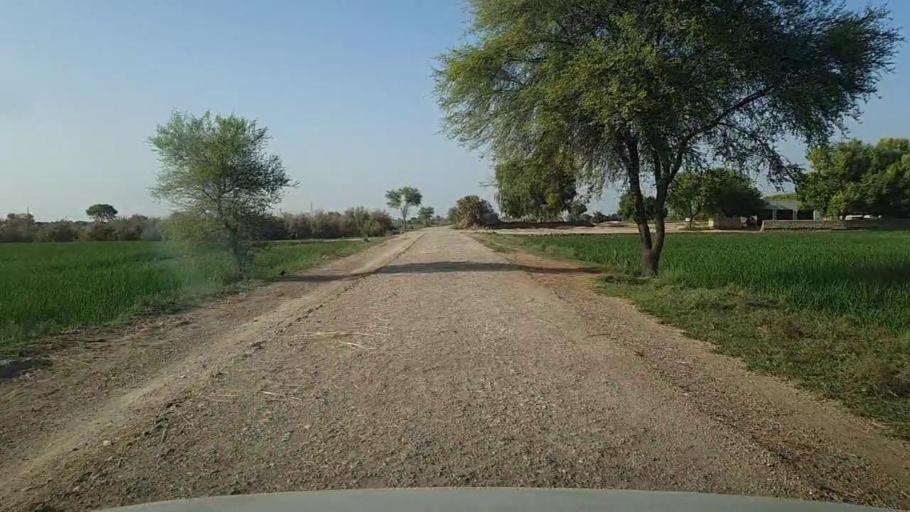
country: PK
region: Sindh
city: Kandhkot
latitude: 28.2998
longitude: 69.3288
